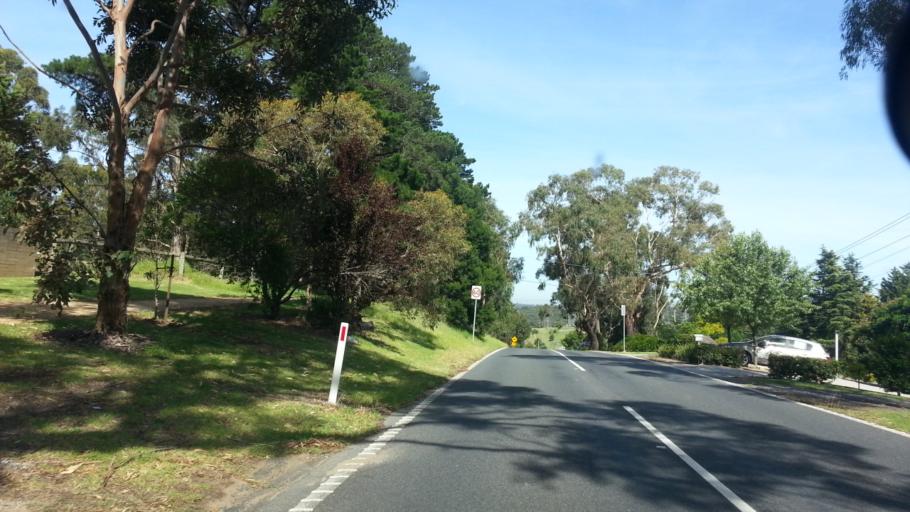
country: AU
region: Victoria
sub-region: Casey
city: Endeavour Hills
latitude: -37.9595
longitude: 145.2740
